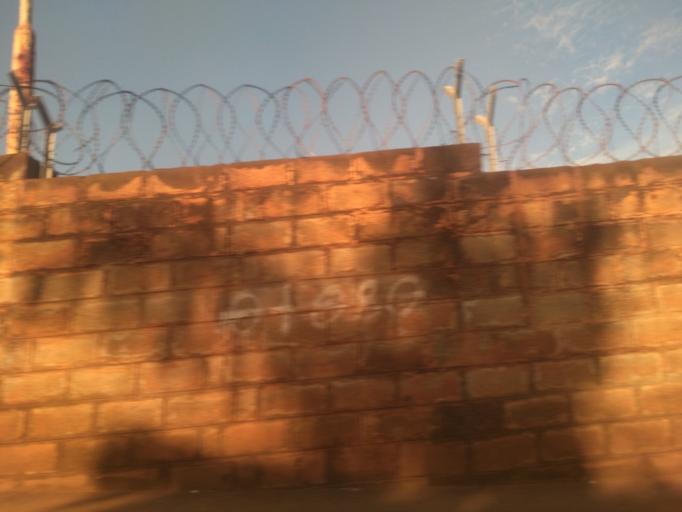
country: UG
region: Central Region
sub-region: Kampala District
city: Kampala
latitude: 0.3137
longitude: 32.5994
